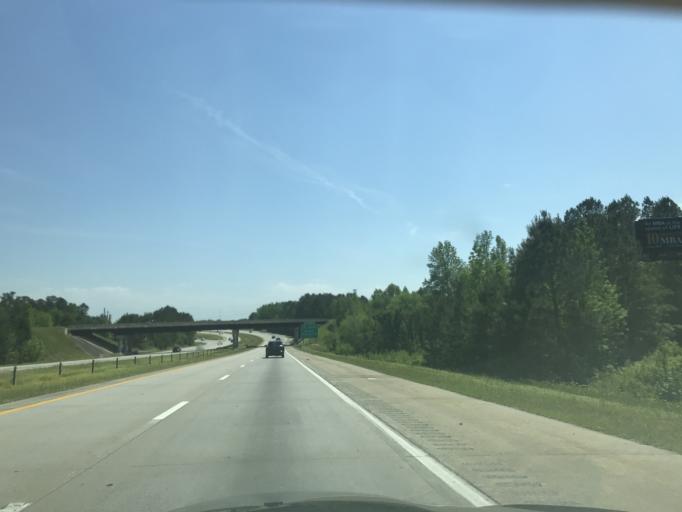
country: US
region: North Carolina
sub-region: Johnston County
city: Benson
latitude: 35.3998
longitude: -78.5230
